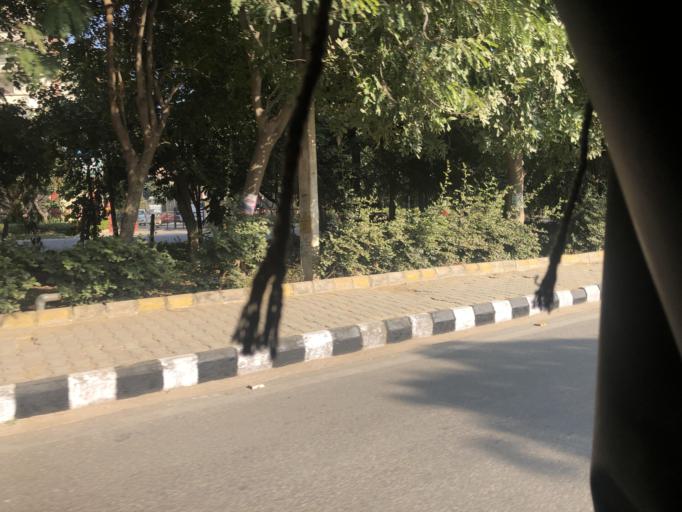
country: IN
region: Haryana
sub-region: Gurgaon
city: Gurgaon
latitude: 28.4519
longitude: 77.0761
